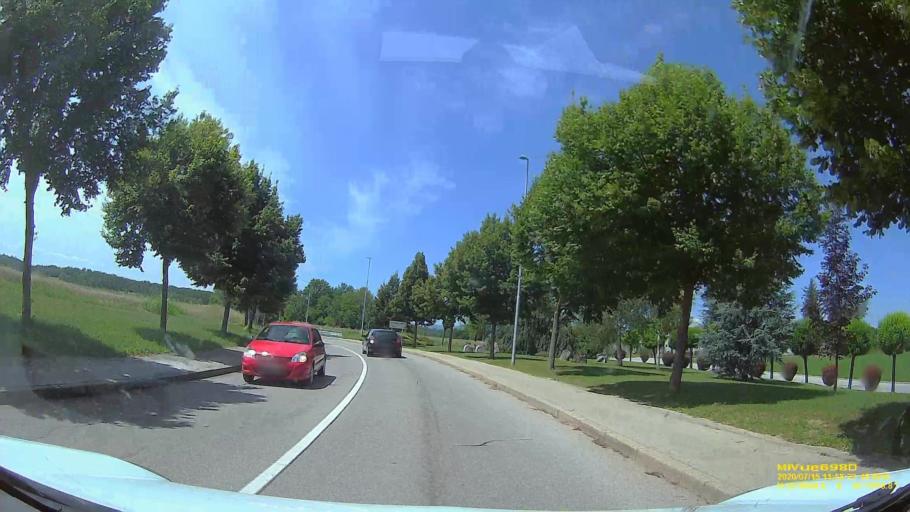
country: SI
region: Metlika
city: Metlika
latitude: 45.6457
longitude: 15.3148
